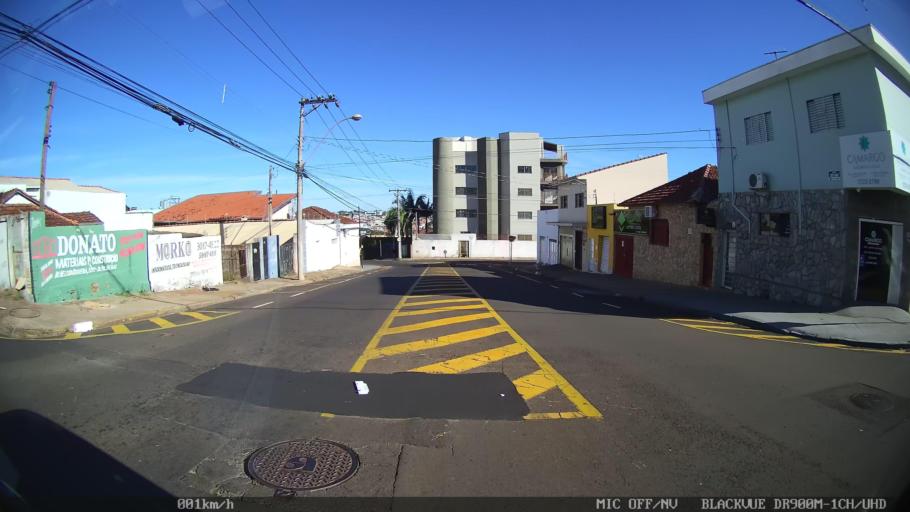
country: BR
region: Sao Paulo
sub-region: Franca
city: Franca
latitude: -20.5316
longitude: -47.4014
